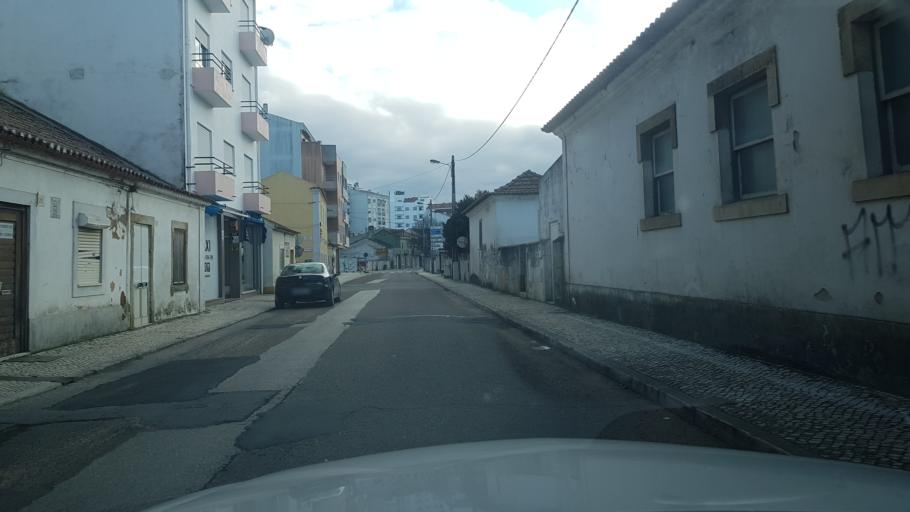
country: PT
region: Santarem
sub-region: Entroncamento
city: Entroncamento
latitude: 39.4638
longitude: -8.4712
